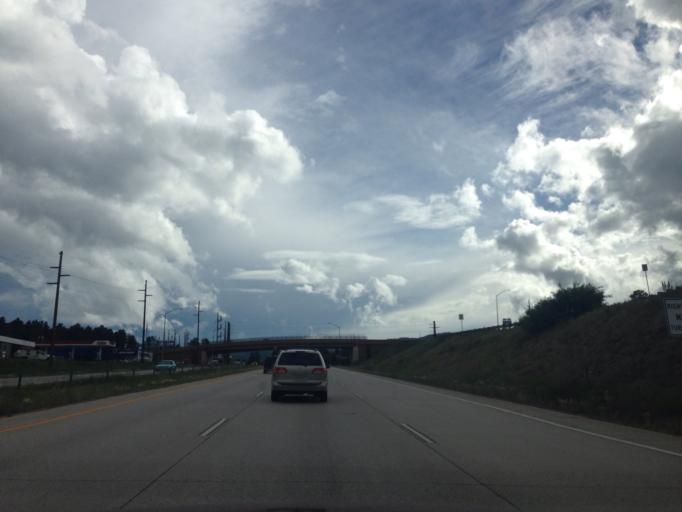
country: US
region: Colorado
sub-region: Jefferson County
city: Evergreen
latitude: 39.5391
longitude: -105.3000
